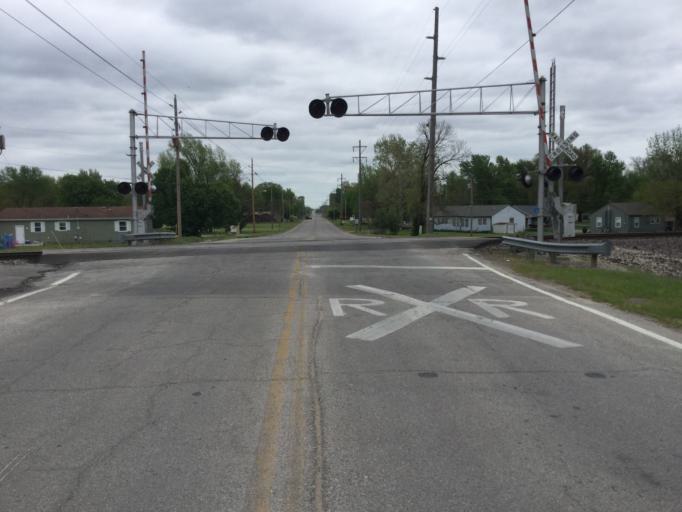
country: US
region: Kansas
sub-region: Labette County
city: Parsons
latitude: 37.3258
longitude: -95.2588
